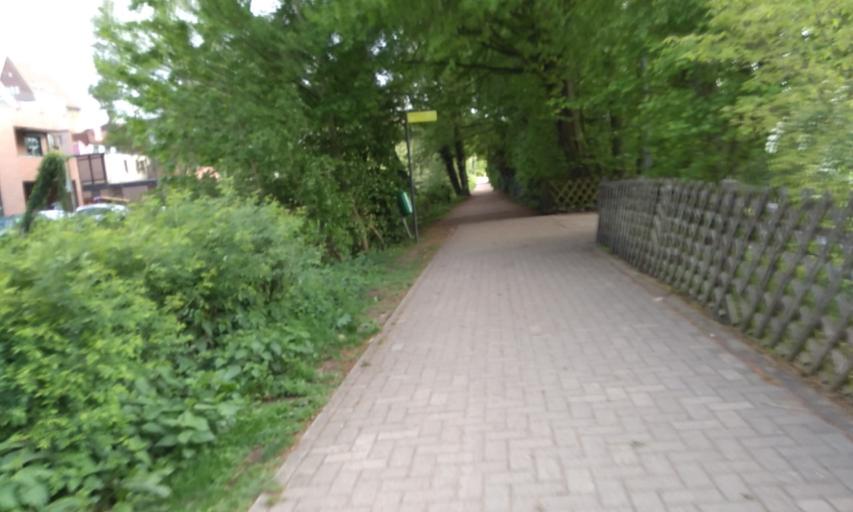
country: DE
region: Lower Saxony
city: Buxtehude
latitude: 53.4777
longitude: 9.6977
